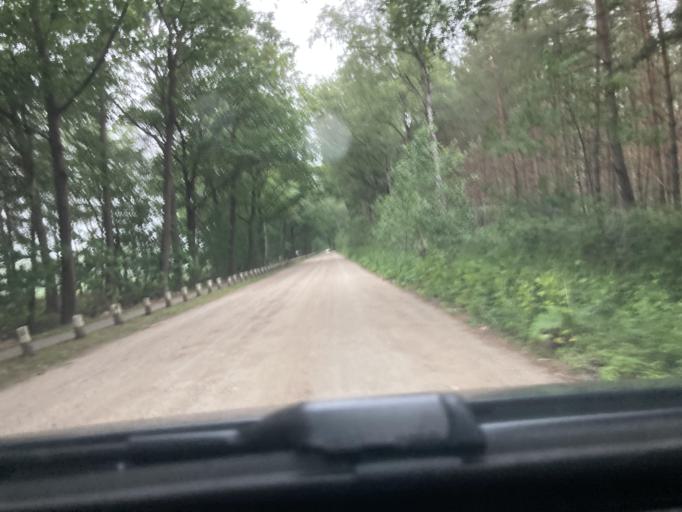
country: NL
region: North Brabant
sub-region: Gemeente Hilvarenbeek
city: Hilvarenbeek
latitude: 51.4367
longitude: 5.1546
